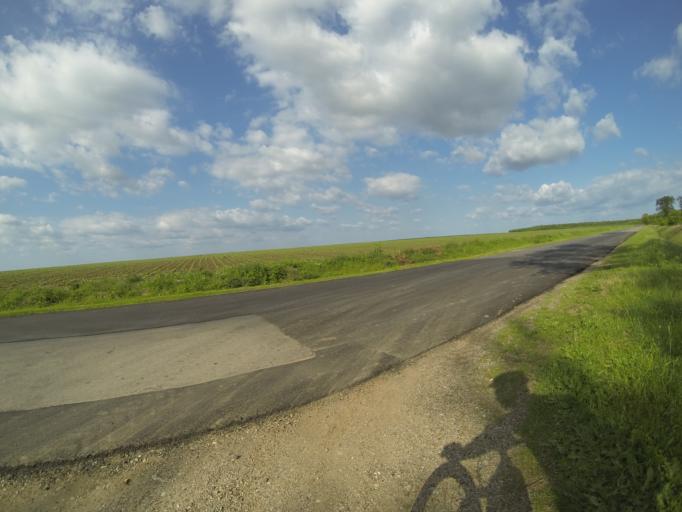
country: RO
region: Dolj
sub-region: Comuna Plenita
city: Castrele Traiane
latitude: 44.2547
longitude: 23.1465
